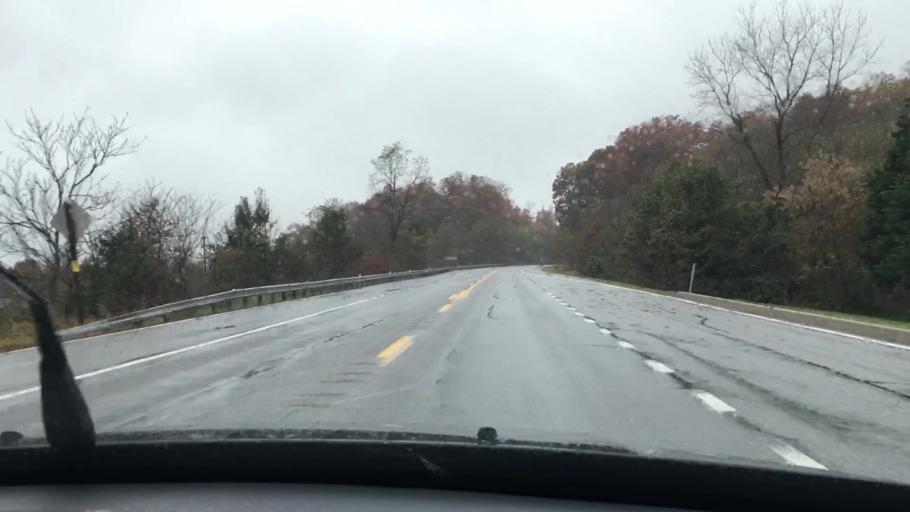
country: US
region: Maryland
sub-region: Frederick County
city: Buckeystown
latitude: 39.3233
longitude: -77.4201
